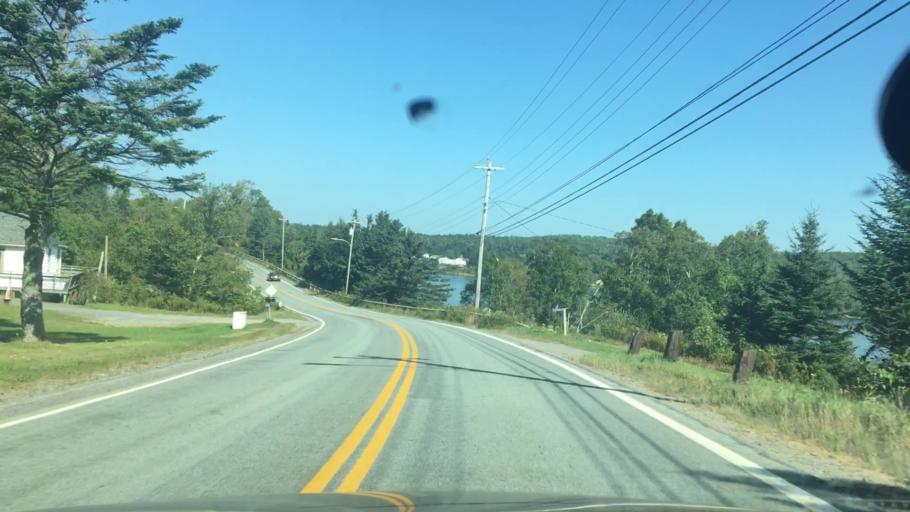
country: CA
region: Nova Scotia
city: New Glasgow
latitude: 44.9152
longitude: -62.5386
